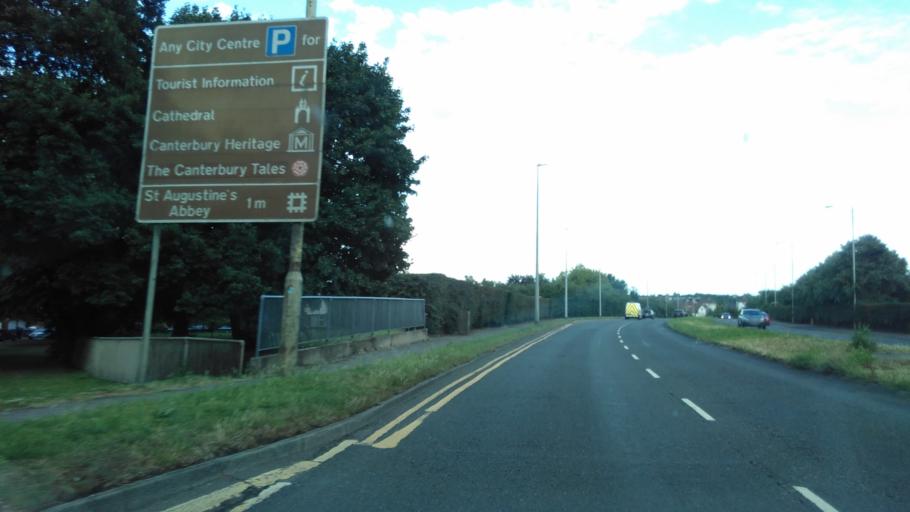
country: GB
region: England
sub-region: Kent
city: Canterbury
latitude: 51.2810
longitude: 1.0681
